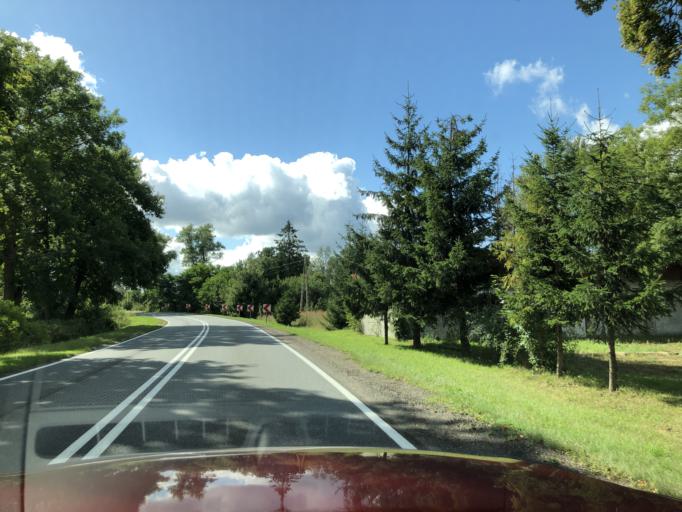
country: PL
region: West Pomeranian Voivodeship
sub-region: Powiat szczecinecki
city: Bialy Bor
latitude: 53.8460
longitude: 16.8295
